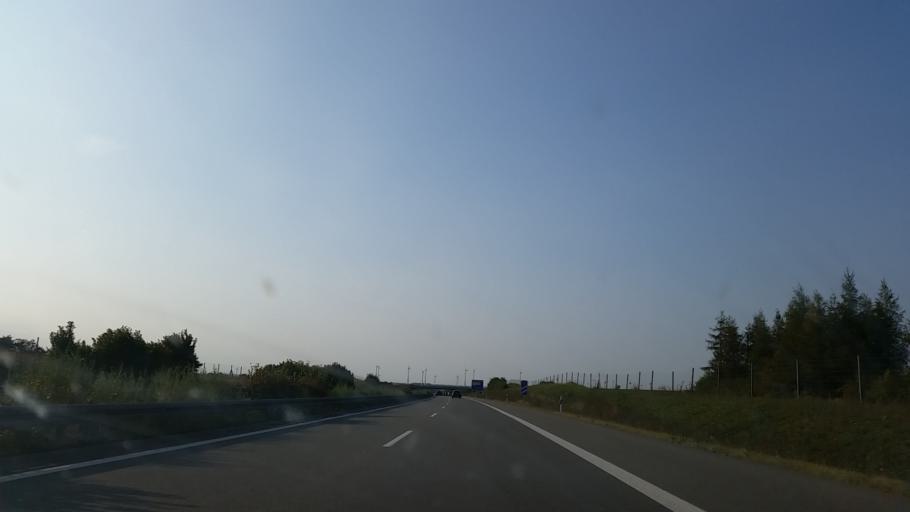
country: DE
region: Mecklenburg-Vorpommern
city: Brunn
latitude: 53.6572
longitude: 13.3619
